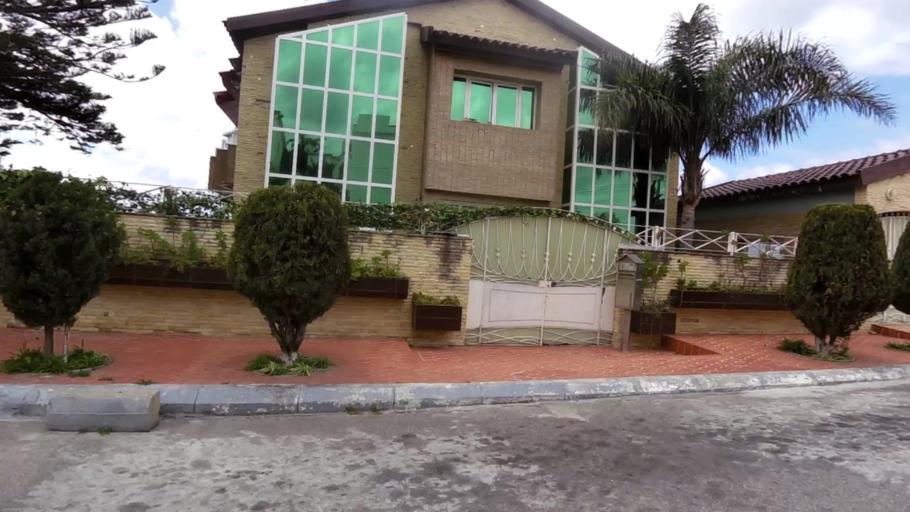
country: MA
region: Tanger-Tetouan
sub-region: Tanger-Assilah
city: Tangier
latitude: 35.7779
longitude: -5.7728
